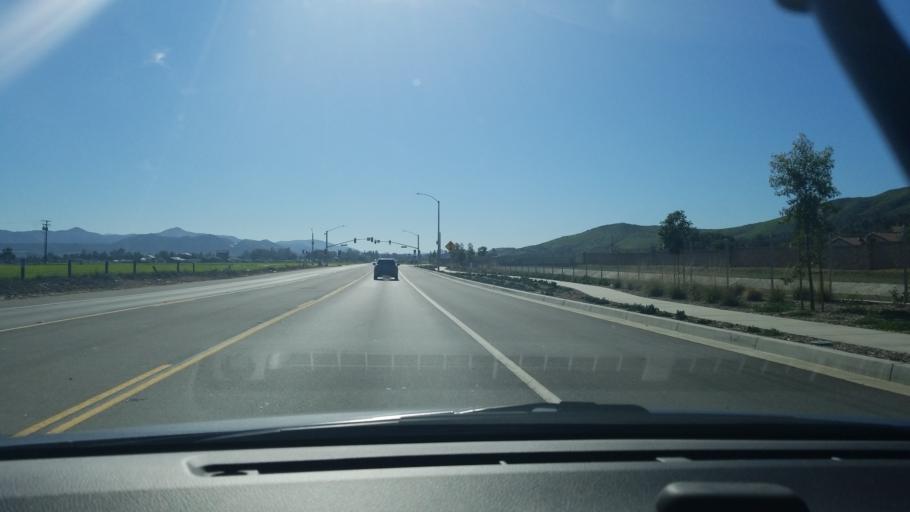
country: US
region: California
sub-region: Riverside County
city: Green Acres
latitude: 33.7311
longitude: -117.0765
